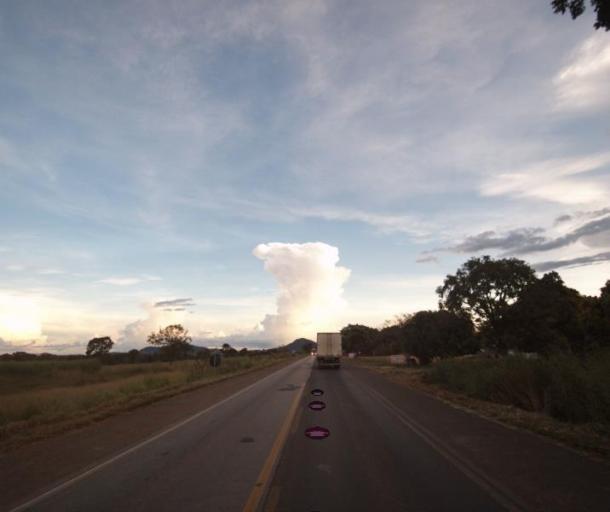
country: BR
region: Goias
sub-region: Uruacu
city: Uruacu
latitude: -14.3366
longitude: -49.1551
